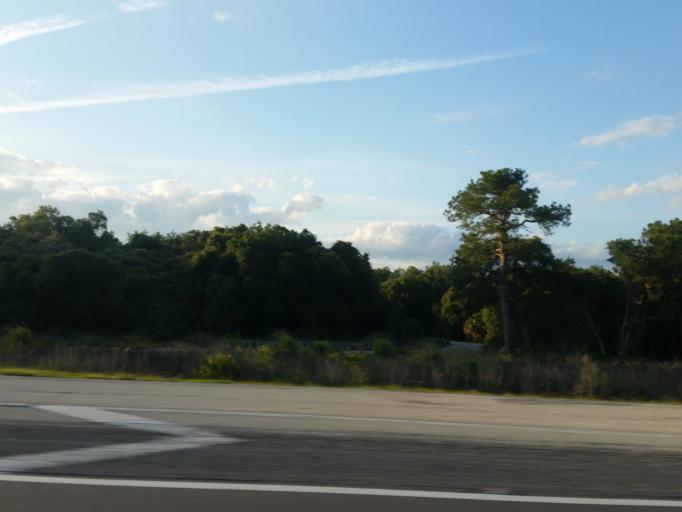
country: US
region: Florida
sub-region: Sarasota County
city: Plantation
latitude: 27.1109
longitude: -82.3436
